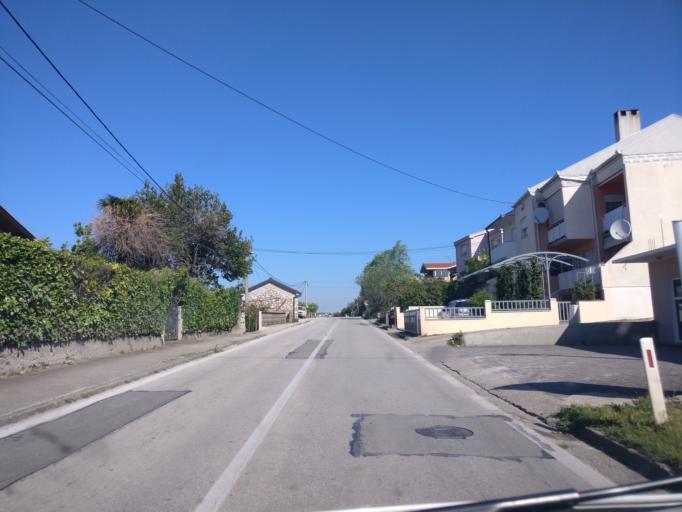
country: BA
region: Federation of Bosnia and Herzegovina
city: Capljina
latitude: 43.1224
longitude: 17.6841
